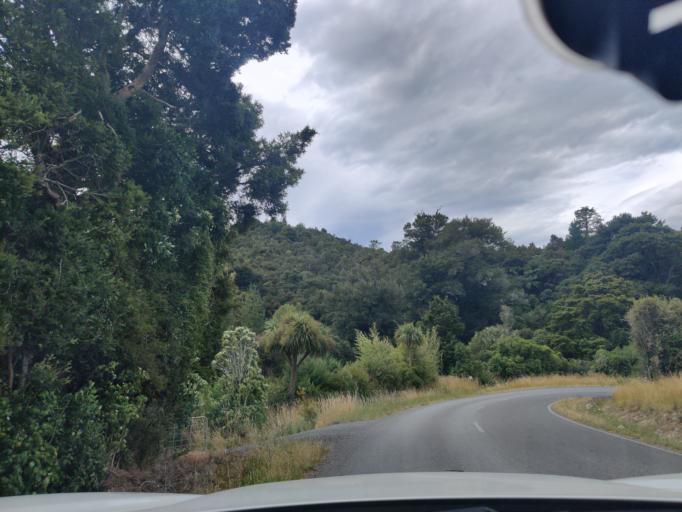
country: NZ
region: Wellington
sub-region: Masterton District
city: Masterton
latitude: -41.0371
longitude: 175.4178
